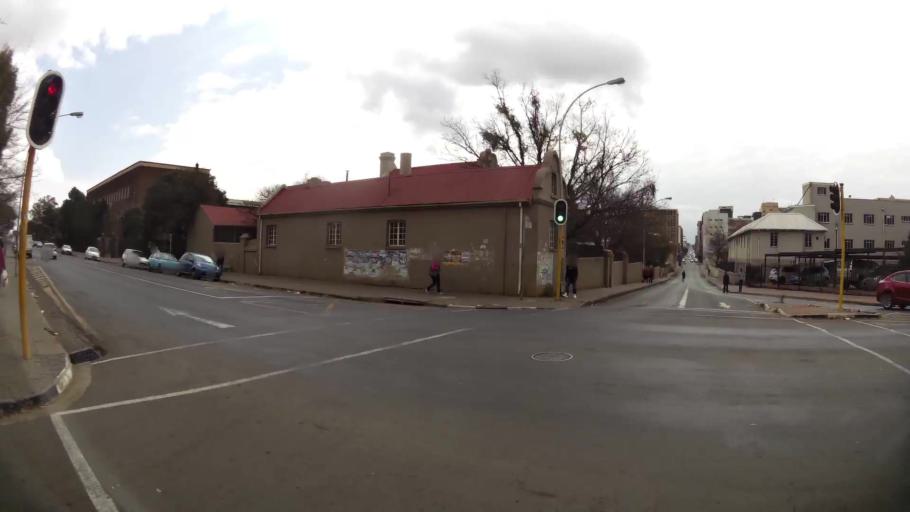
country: ZA
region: Orange Free State
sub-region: Mangaung Metropolitan Municipality
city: Bloemfontein
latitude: -29.1205
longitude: 26.2174
